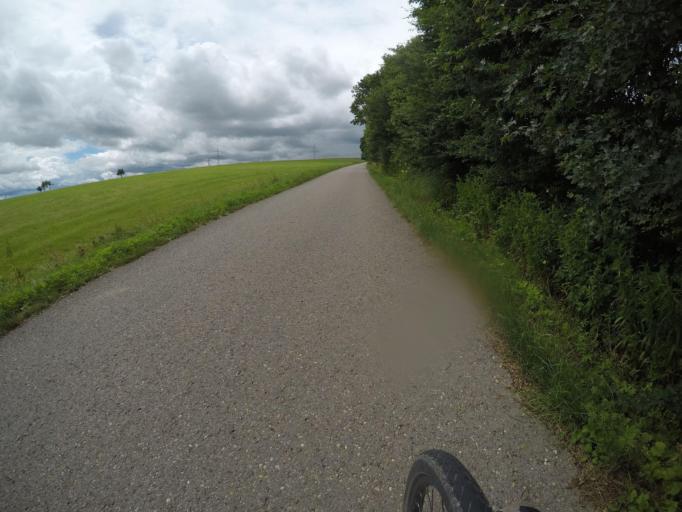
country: DE
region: Baden-Wuerttemberg
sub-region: Regierungsbezirk Stuttgart
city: Unterjettingen
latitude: 48.5756
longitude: 8.7965
